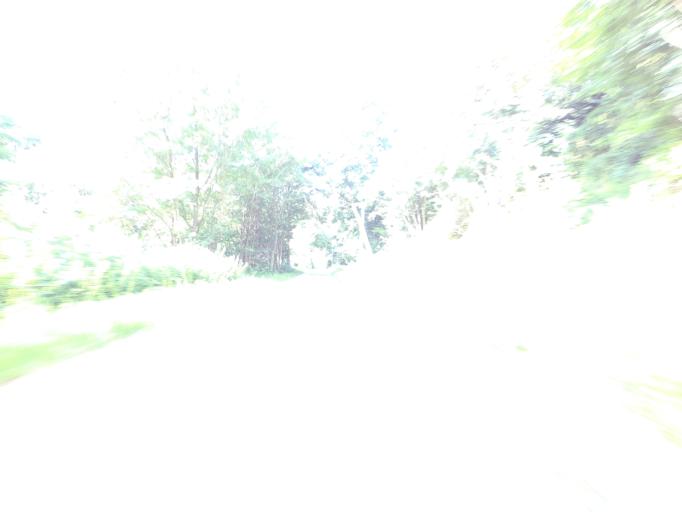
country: DK
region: Central Jutland
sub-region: Silkeborg Kommune
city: Silkeborg
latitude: 56.1644
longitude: 9.5572
